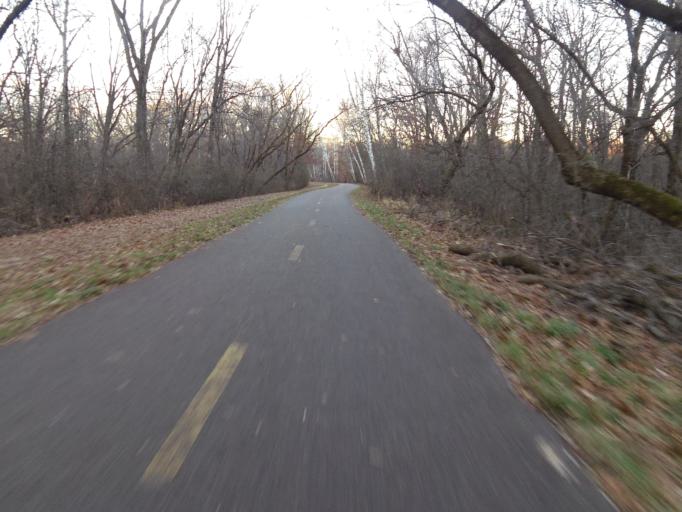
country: US
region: Minnesota
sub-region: Washington County
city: Grant
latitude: 45.0717
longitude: -92.9081
